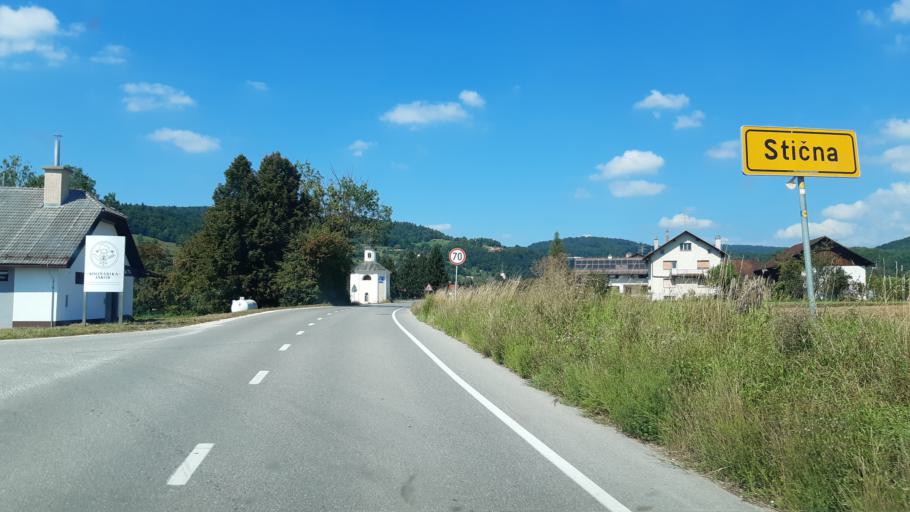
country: SI
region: Ivancna Gorica
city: Ivancna Gorica
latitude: 45.9470
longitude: 14.8028
